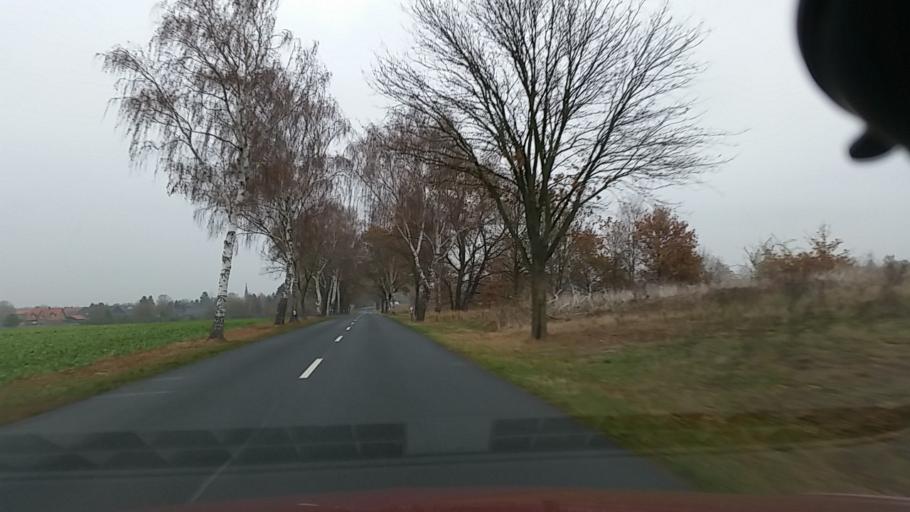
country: DE
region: Lower Saxony
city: Stadensen
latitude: 52.8743
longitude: 10.5807
